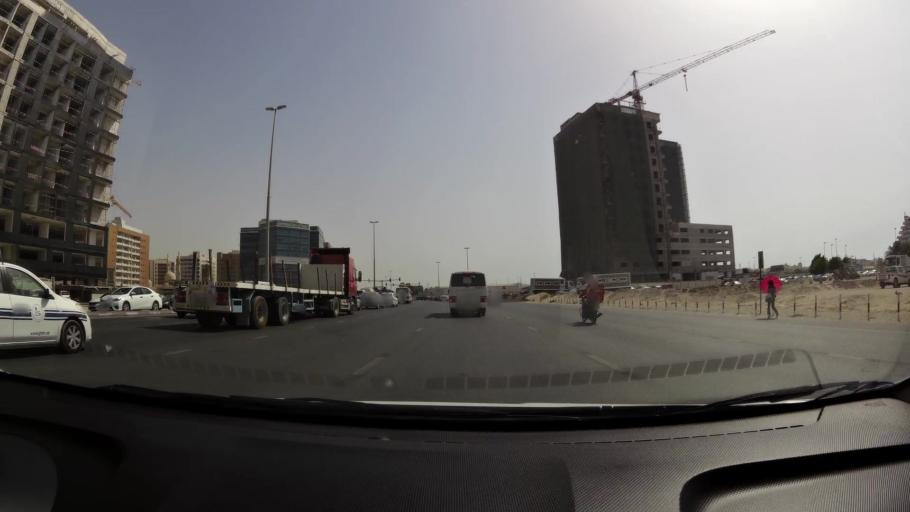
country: AE
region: Ash Shariqah
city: Sharjah
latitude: 25.2898
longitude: 55.4017
